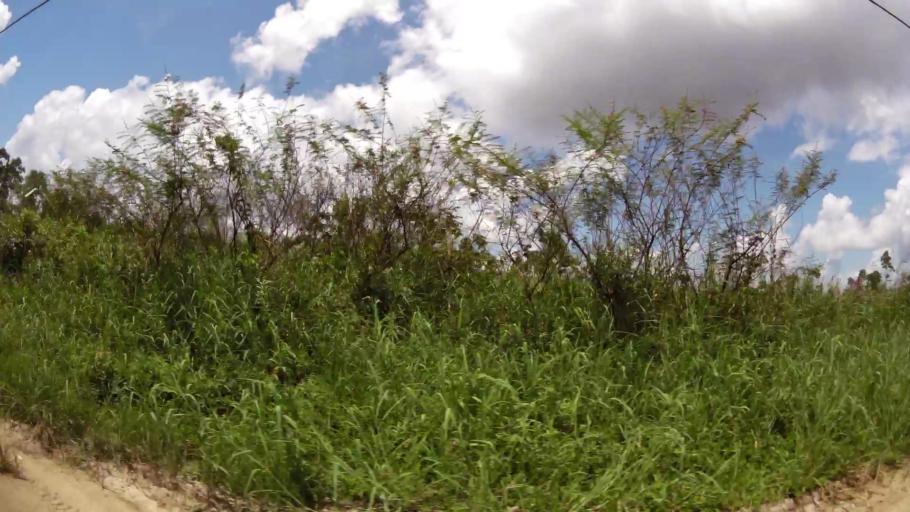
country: SR
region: Paramaribo
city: Paramaribo
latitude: 5.8035
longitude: -55.1268
